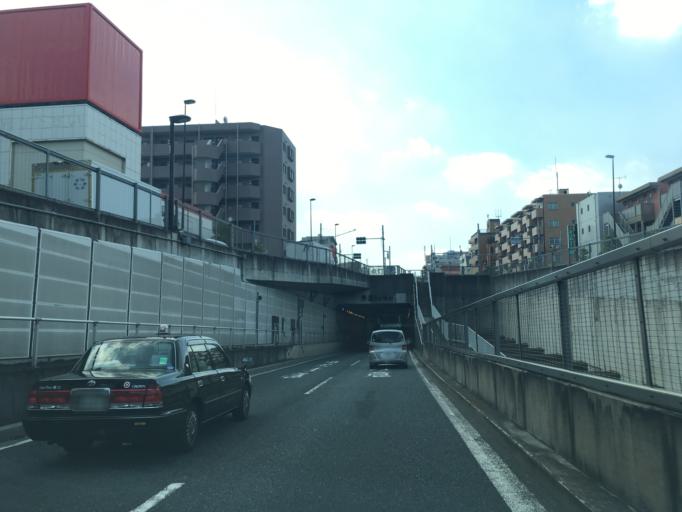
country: JP
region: Saitama
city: Wako
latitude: 35.7326
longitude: 139.6146
